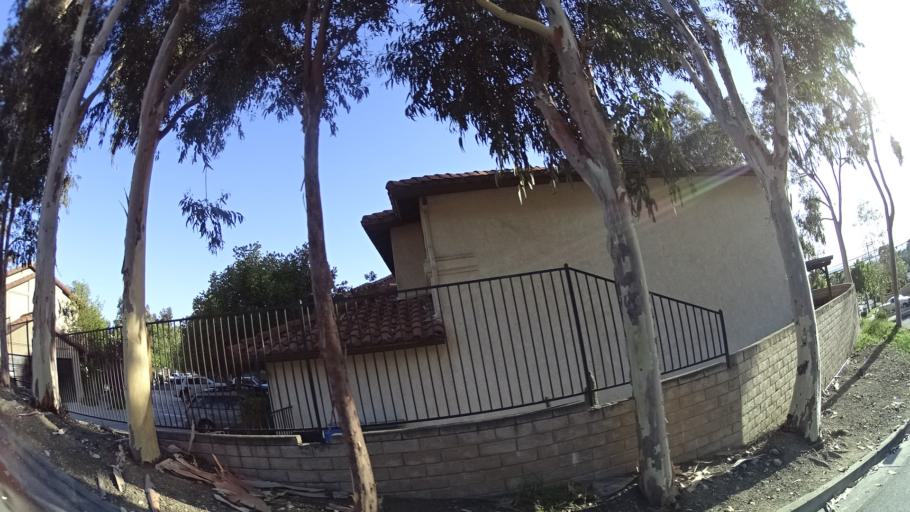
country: US
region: California
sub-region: Los Angeles County
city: La Crescenta-Montrose
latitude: 34.2718
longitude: -118.3025
